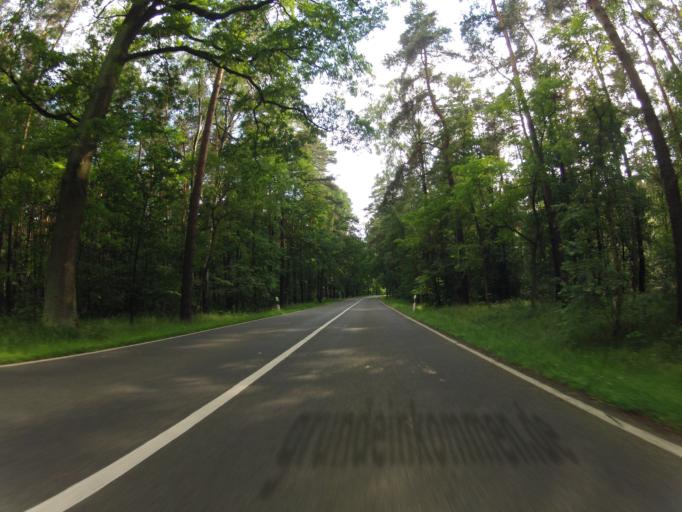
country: DE
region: Saxony
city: Schildau
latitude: 51.4276
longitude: 12.9178
